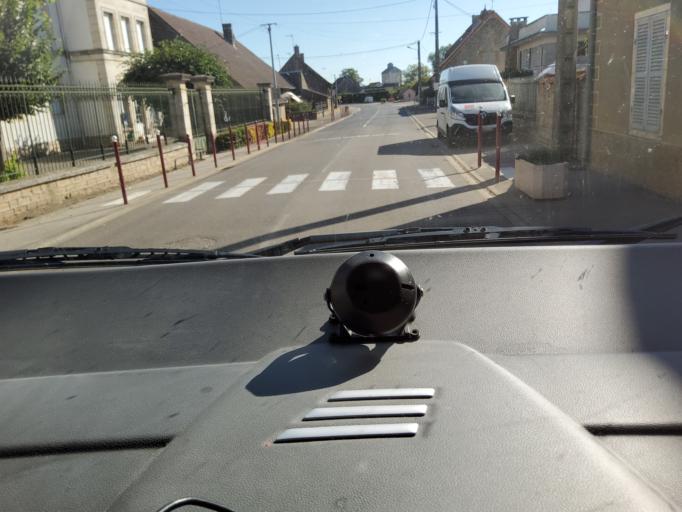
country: FR
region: Bourgogne
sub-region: Departement de la Cote-d'Or
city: Auxonne
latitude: 47.1365
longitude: 5.3400
